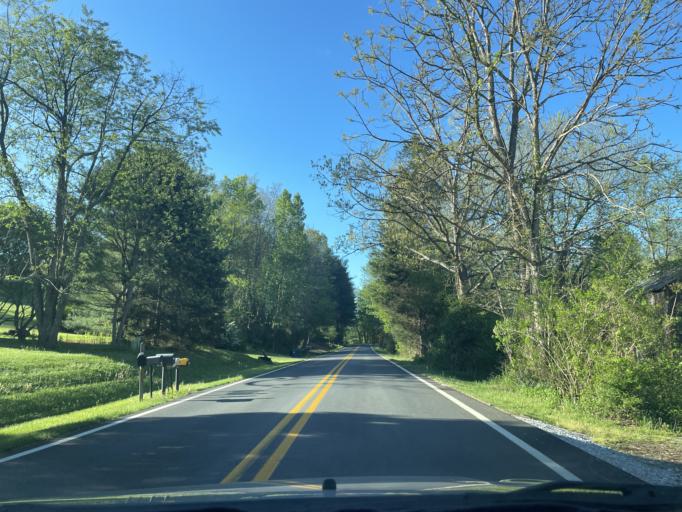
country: US
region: Maryland
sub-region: Carroll County
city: Mount Airy
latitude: 39.4146
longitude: -77.1375
